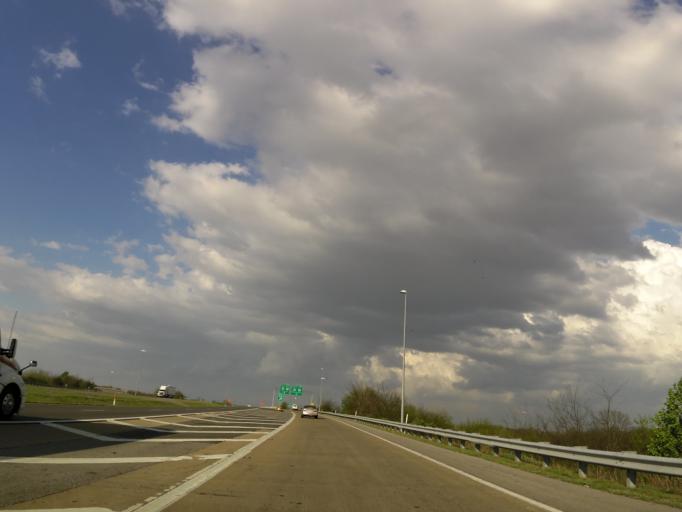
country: US
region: Tennessee
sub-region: Rutherford County
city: Murfreesboro
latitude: 35.9002
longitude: -86.4533
